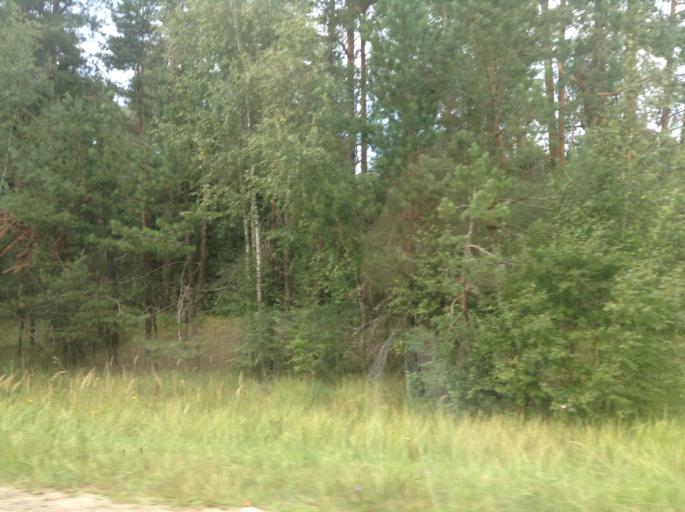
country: RU
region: Moskovskaya
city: Yegor'yevsk
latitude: 55.3513
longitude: 39.1425
